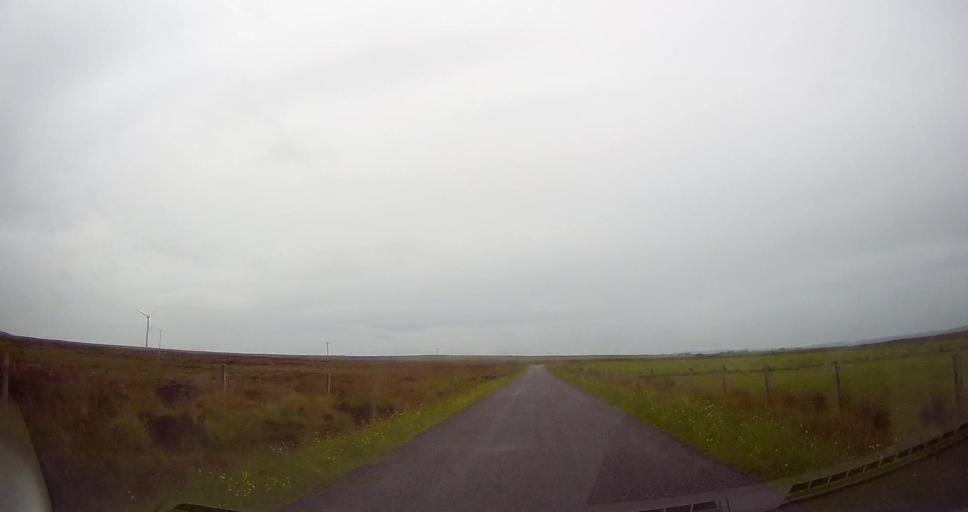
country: GB
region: Scotland
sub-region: Orkney Islands
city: Stromness
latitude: 59.0838
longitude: -3.1903
